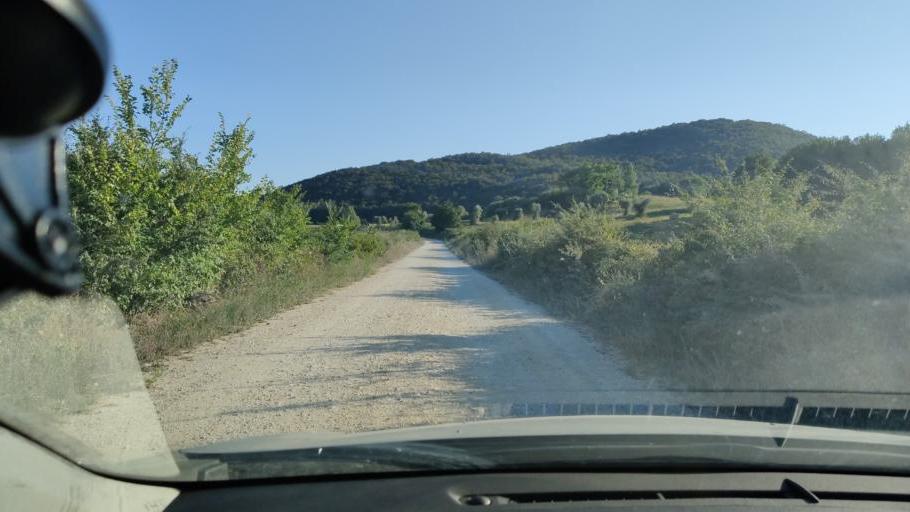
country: IT
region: Umbria
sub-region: Provincia di Terni
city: Amelia
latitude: 42.5443
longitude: 12.3875
